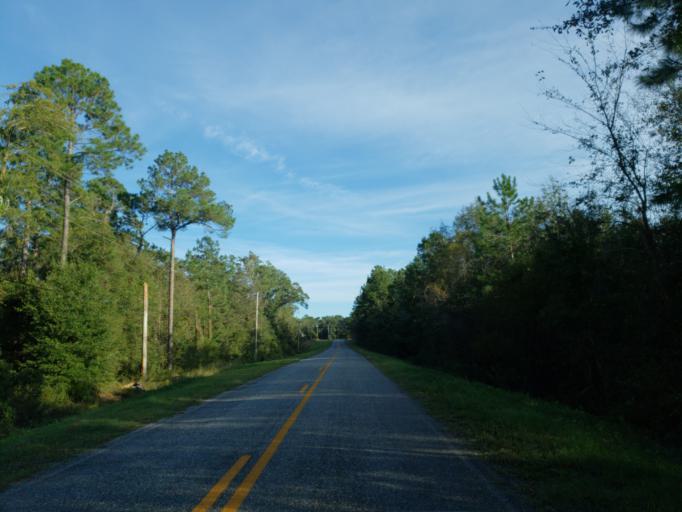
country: US
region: Georgia
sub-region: Crisp County
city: Cordele
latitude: 32.0187
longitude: -83.7355
